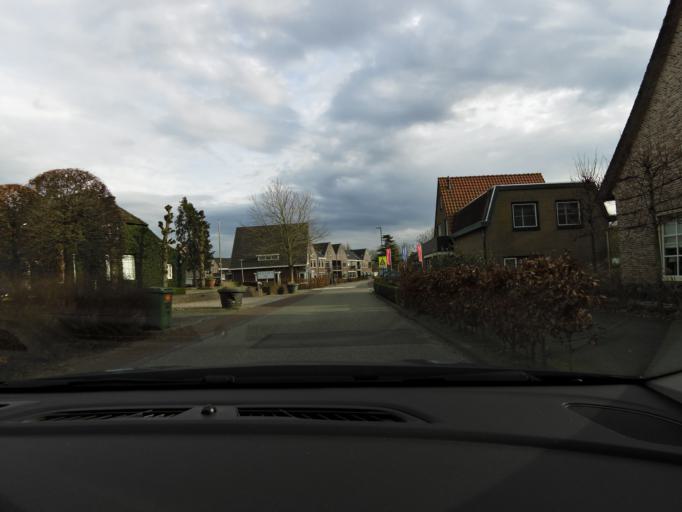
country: NL
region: South Holland
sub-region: Gemeente Gorinchem
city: Gorinchem
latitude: 51.8796
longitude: 4.9467
